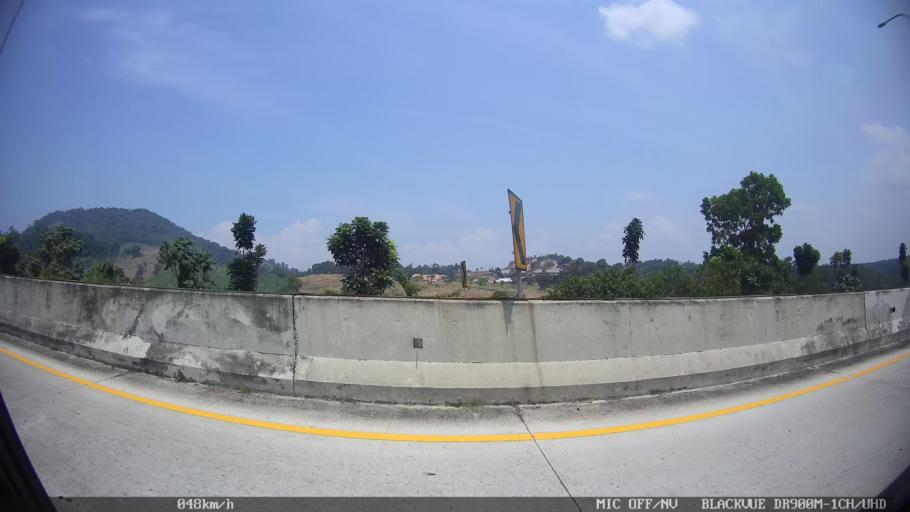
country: ID
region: Lampung
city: Panjang
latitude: -5.4001
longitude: 105.3460
